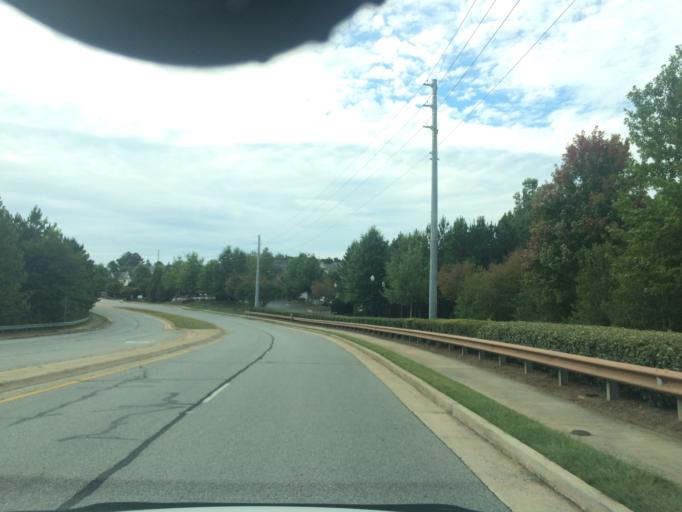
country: US
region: Georgia
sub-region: Cobb County
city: Kennesaw
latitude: 34.0535
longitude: -84.5874
